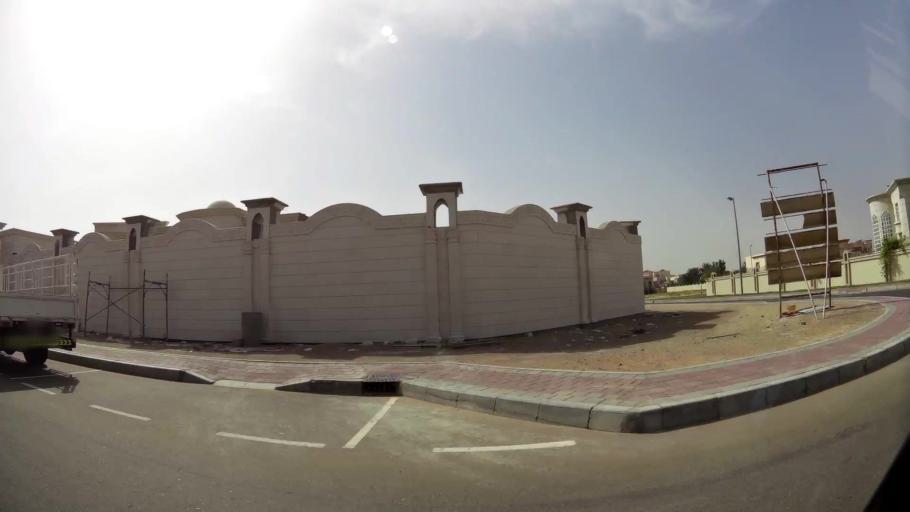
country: AE
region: Abu Dhabi
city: Al Ain
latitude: 24.1515
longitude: 55.7019
